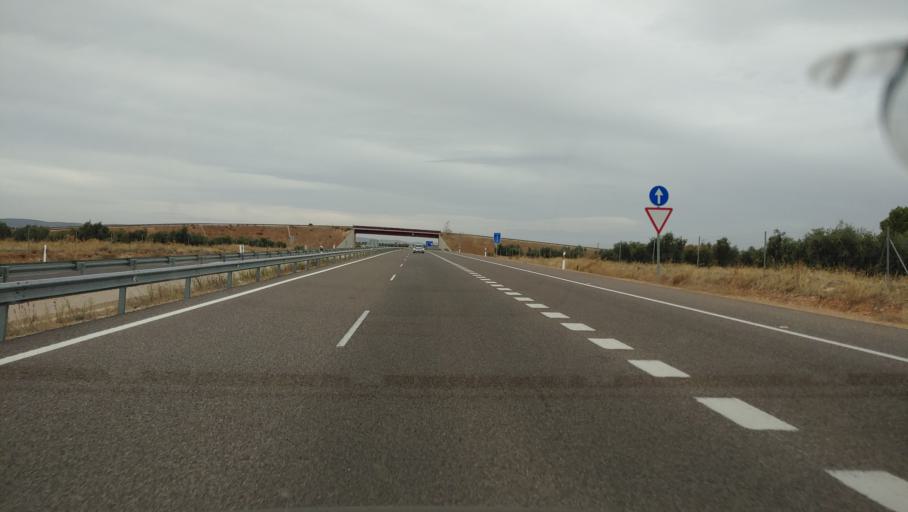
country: ES
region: Castille-La Mancha
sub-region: Provincia de Ciudad Real
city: Valenzuela de Calatrava
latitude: 38.9003
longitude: -3.8189
